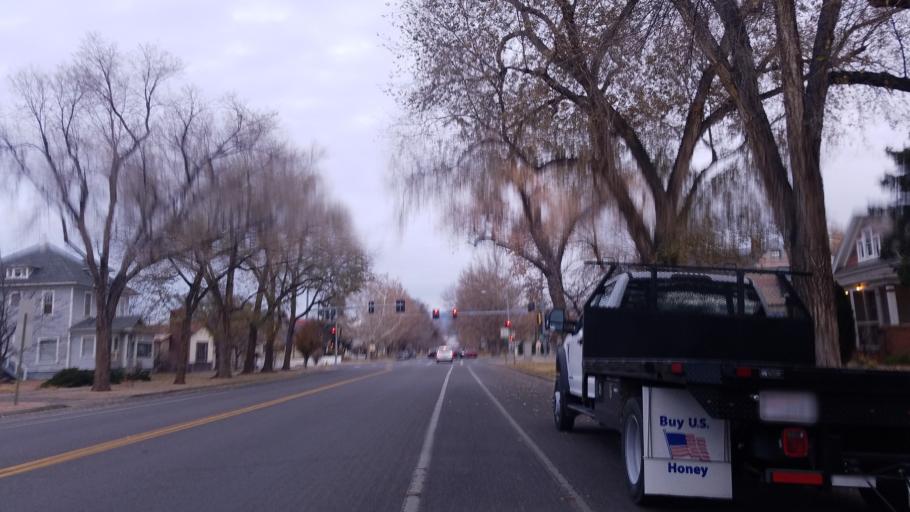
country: US
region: Colorado
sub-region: Mesa County
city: Grand Junction
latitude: 39.0673
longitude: -108.5536
